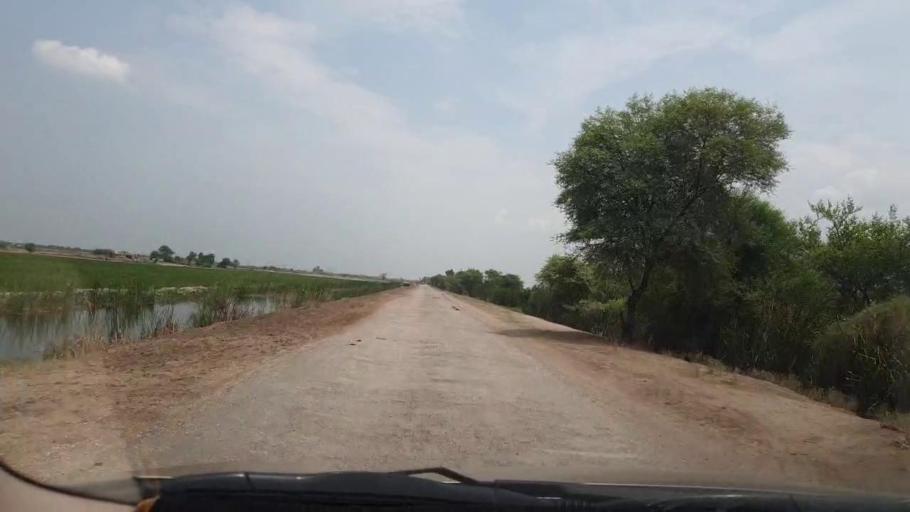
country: PK
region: Sindh
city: Larkana
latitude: 27.6074
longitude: 68.1639
